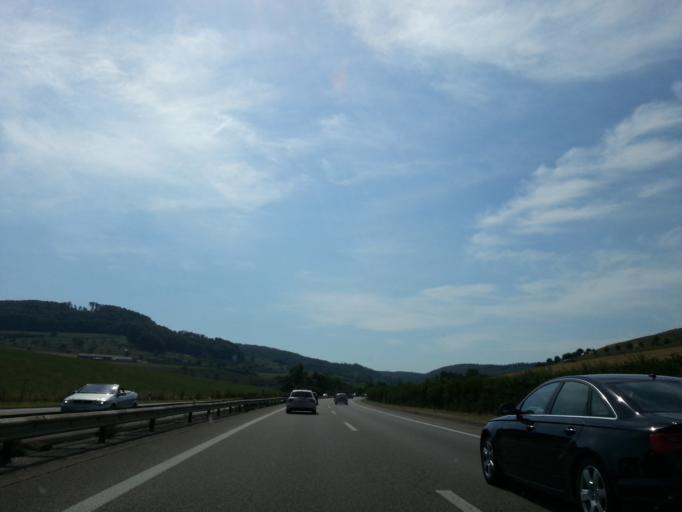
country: CH
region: Basel-Landschaft
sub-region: Bezirk Liestal
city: Arisdorf
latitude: 47.5134
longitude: 7.7591
